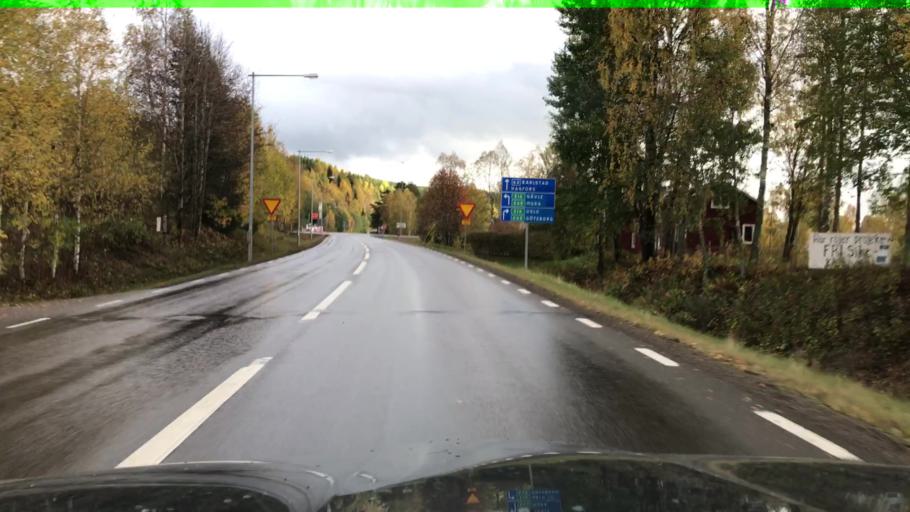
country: SE
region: Vaermland
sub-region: Hagfors Kommun
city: Ekshaerad
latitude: 60.4242
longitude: 13.2544
